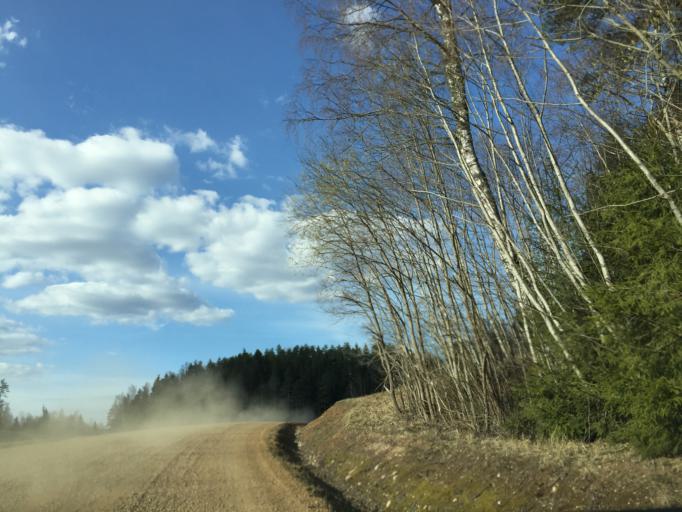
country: EE
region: Tartu
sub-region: Elva linn
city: Elva
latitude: 58.0993
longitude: 26.5075
